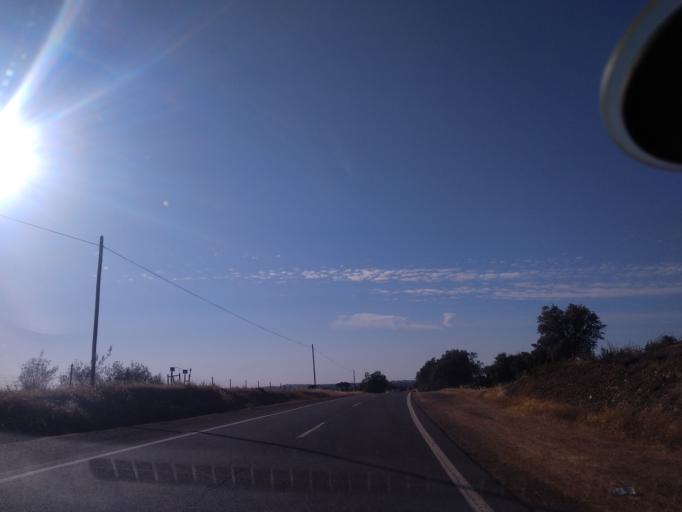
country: PT
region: Beja
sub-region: Almodovar
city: Almodovar
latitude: 37.4628
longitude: -8.0027
